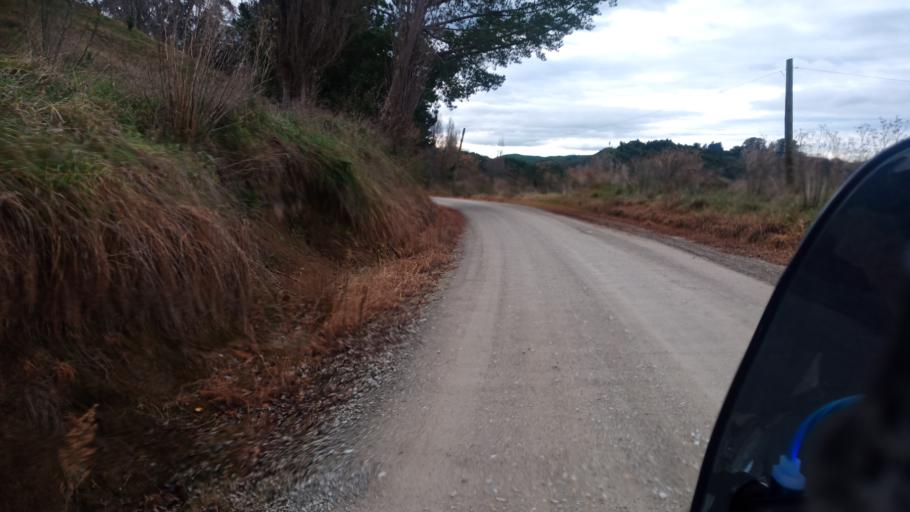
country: NZ
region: Gisborne
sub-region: Gisborne District
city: Gisborne
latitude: -38.3902
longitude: 177.9558
